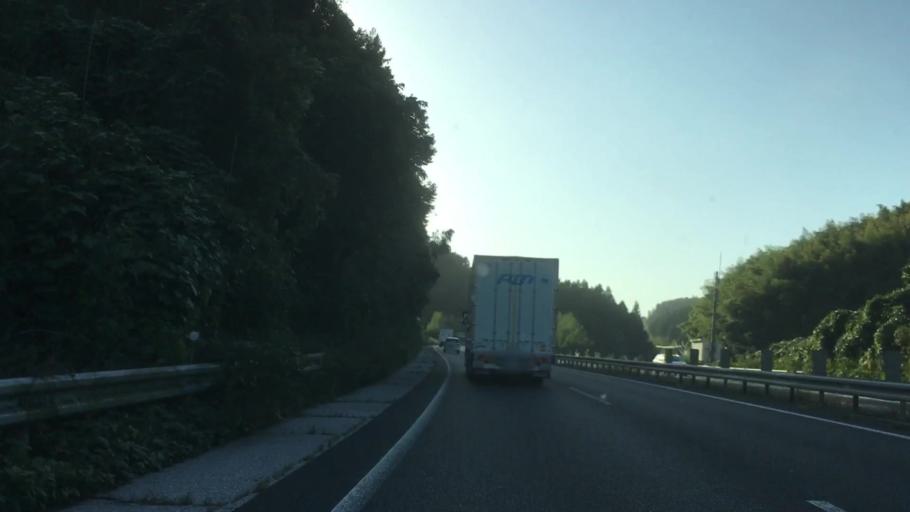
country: JP
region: Yamaguchi
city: Onoda
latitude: 34.1166
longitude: 131.1247
